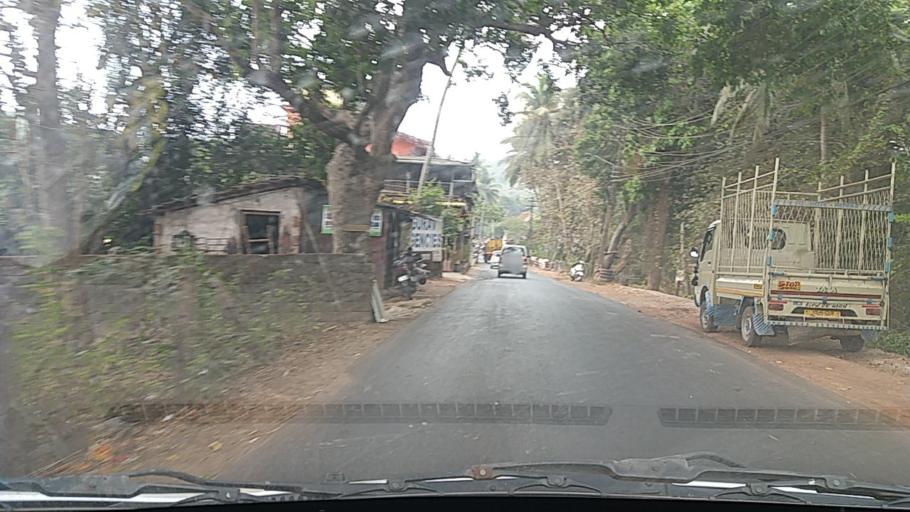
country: IN
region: Goa
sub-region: North Goa
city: Saligao
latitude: 15.5418
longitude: 73.7896
